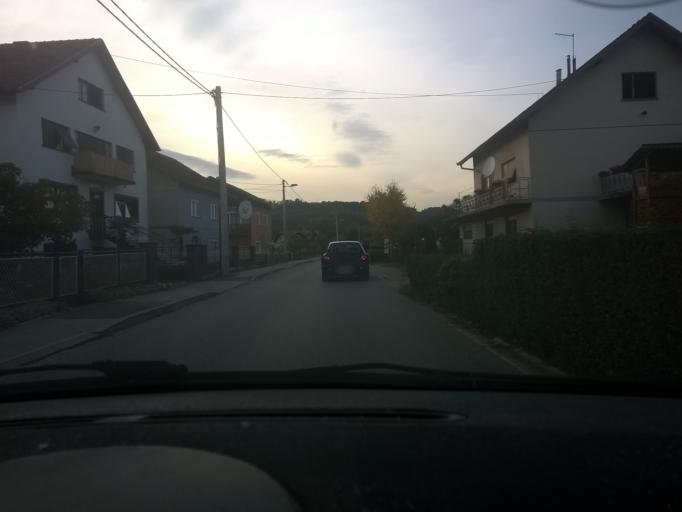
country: HR
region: Krapinsko-Zagorska
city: Zabok
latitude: 46.0778
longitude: 15.9045
